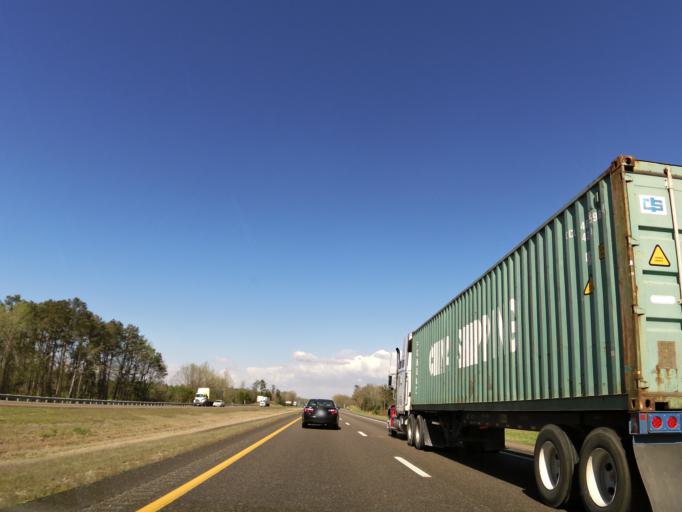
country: US
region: Tennessee
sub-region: Humphreys County
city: New Johnsonville
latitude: 35.8560
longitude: -88.0569
